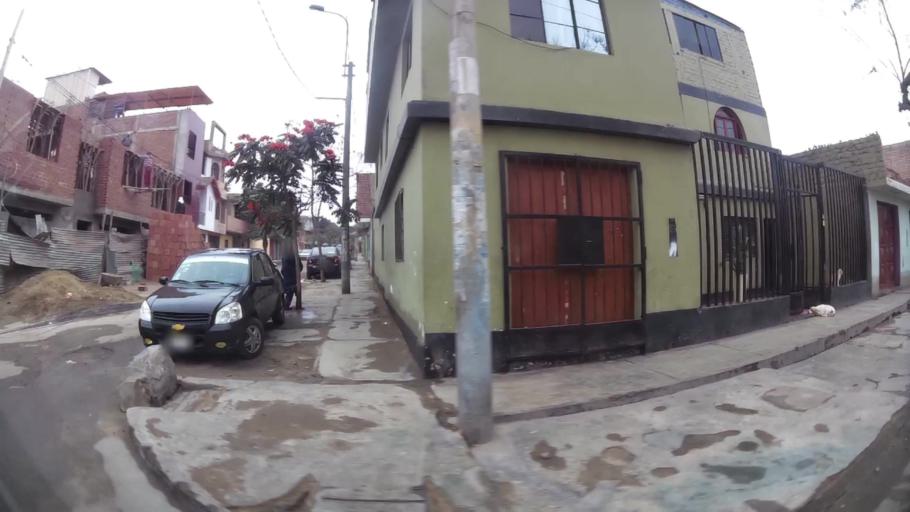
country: PE
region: Lima
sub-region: Lima
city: Surco
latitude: -12.1524
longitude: -76.9679
